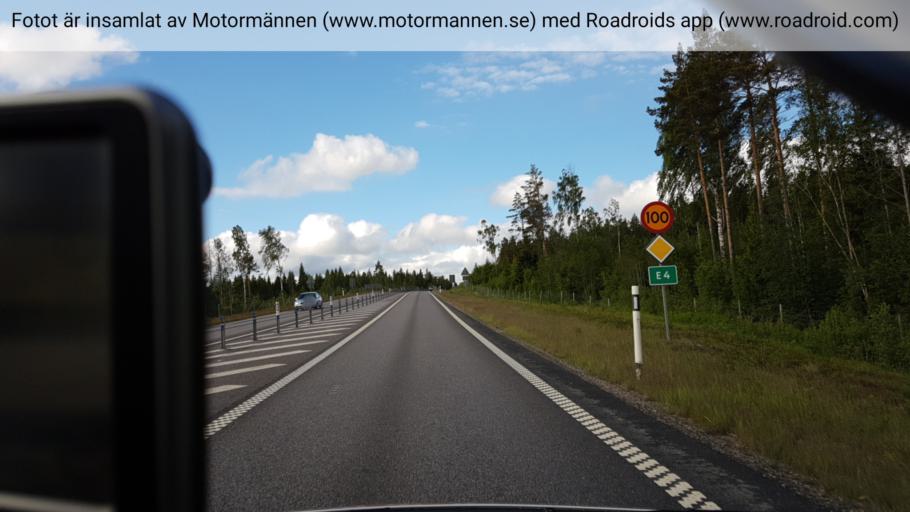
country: SE
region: Vaesternorrland
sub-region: Sundsvalls Kommun
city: Njurundabommen
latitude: 62.0946
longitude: 17.3050
